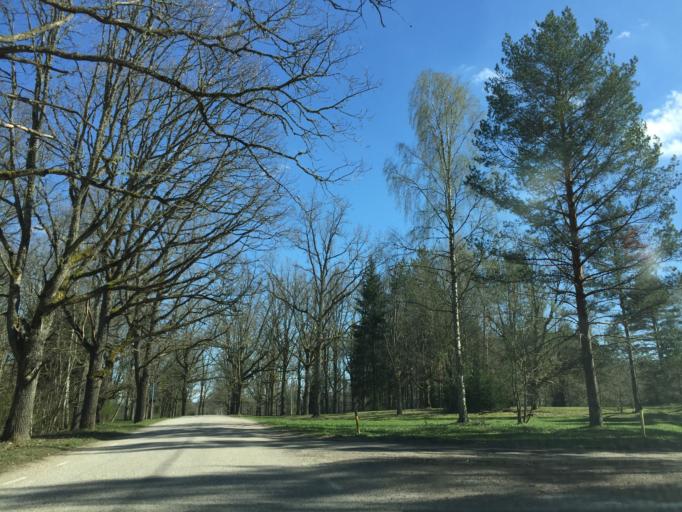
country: EE
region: Valgamaa
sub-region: Valga linn
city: Valga
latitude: 57.8527
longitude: 26.1228
